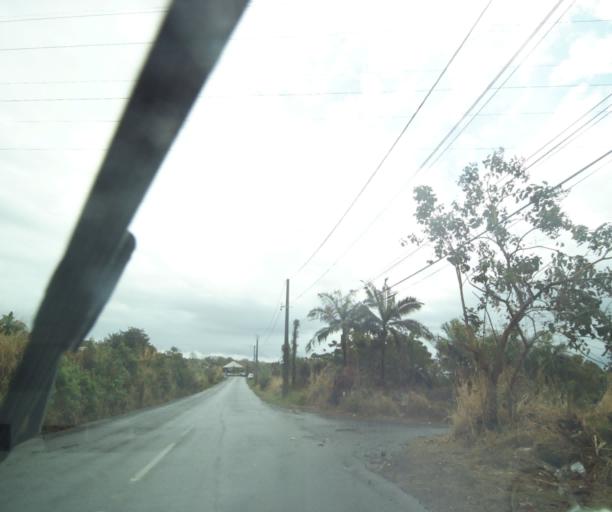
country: RE
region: Reunion
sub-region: Reunion
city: Saint-Paul
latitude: -21.0148
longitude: 55.3077
